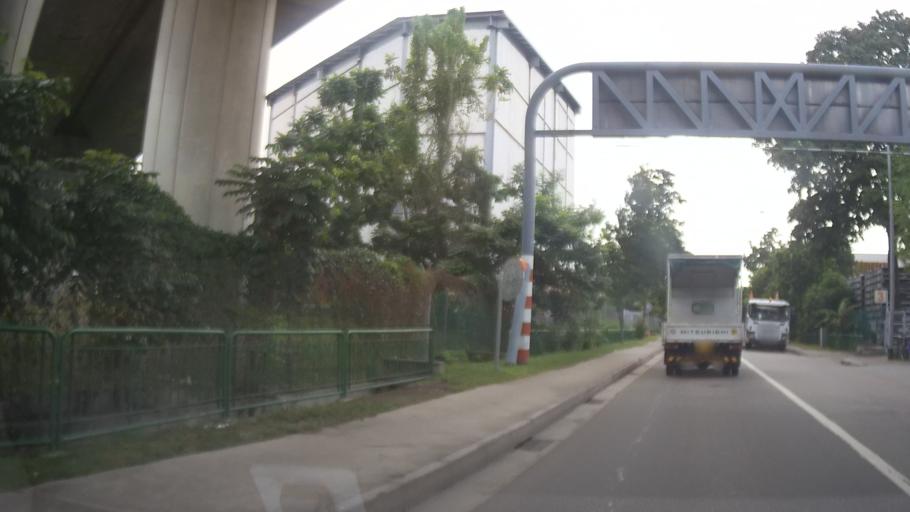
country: MY
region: Johor
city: Johor Bahru
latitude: 1.4193
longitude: 103.7487
